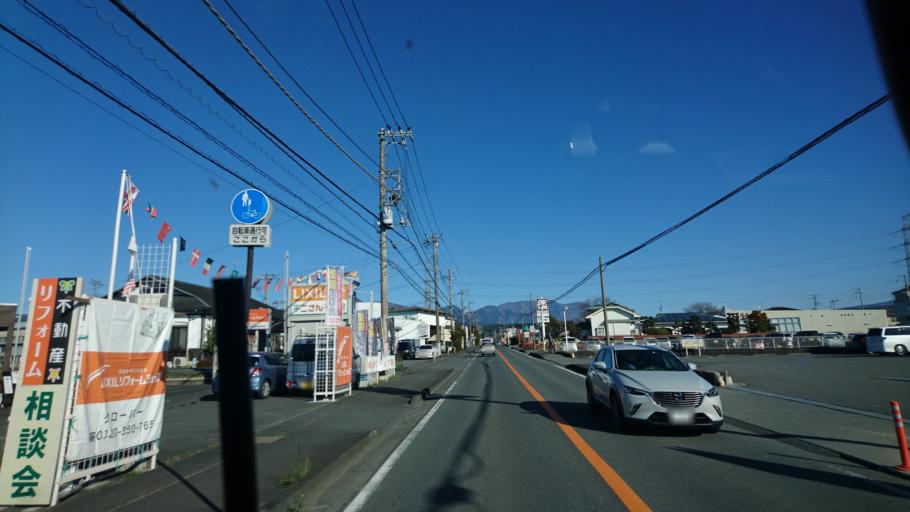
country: JP
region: Shizuoka
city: Fujinomiya
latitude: 35.2513
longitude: 138.6099
